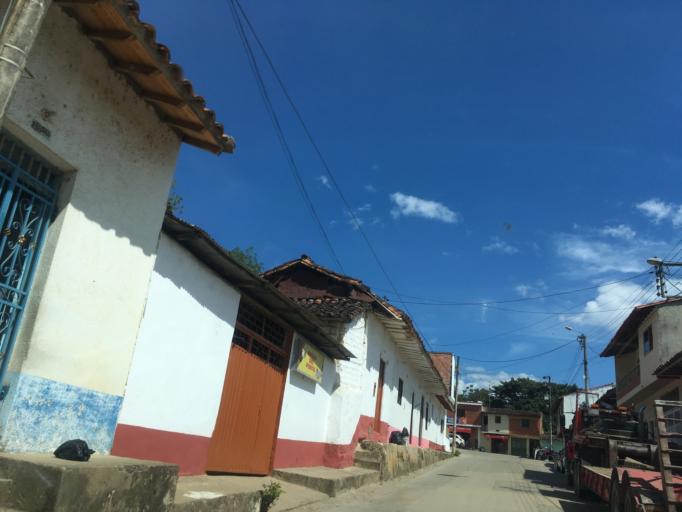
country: CO
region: Santander
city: Coromoro
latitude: 6.2852
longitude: -73.1515
